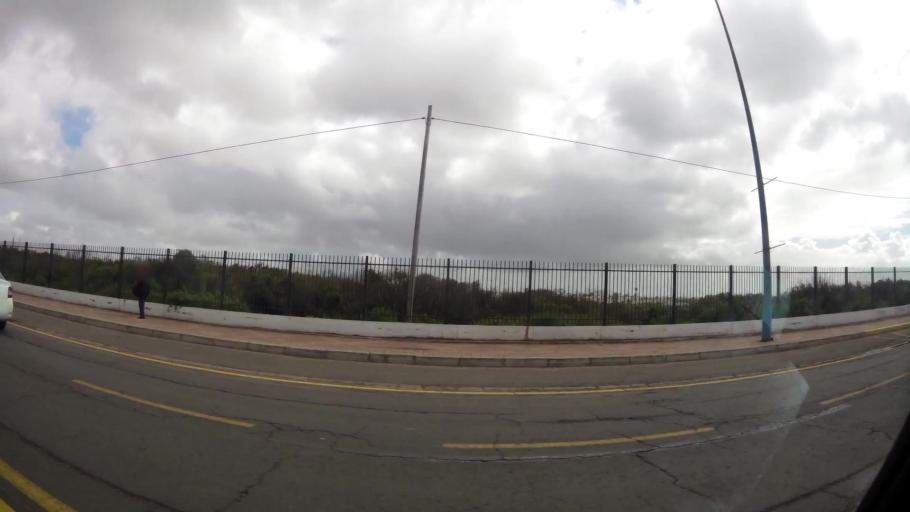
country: MA
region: Grand Casablanca
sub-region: Casablanca
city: Casablanca
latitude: 33.5824
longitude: -7.6961
